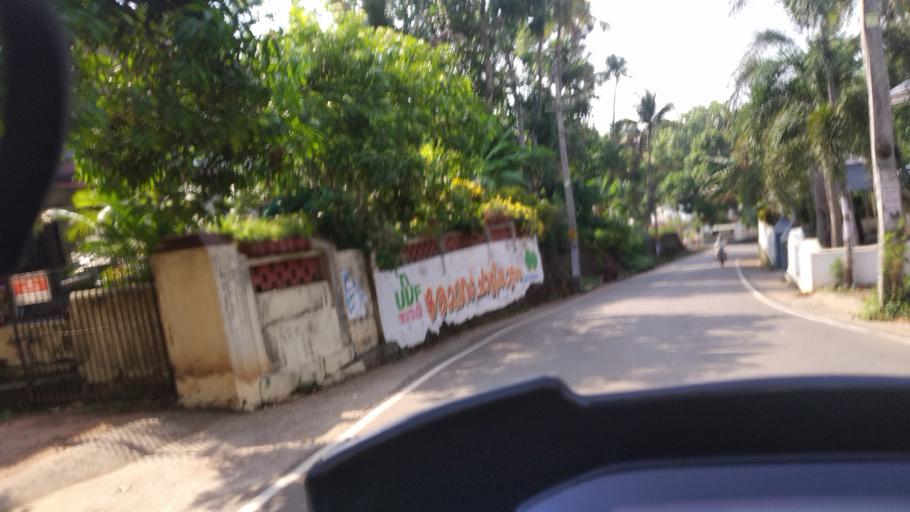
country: IN
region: Kerala
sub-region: Ernakulam
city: Piravam
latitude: 9.8731
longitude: 76.4966
